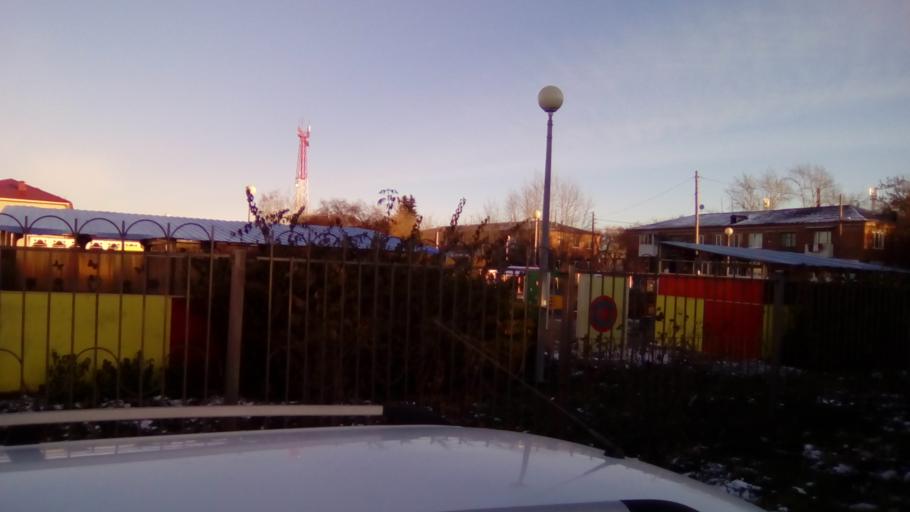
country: RU
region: Tjumen
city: Moskovskiy
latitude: 57.2213
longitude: 65.3556
